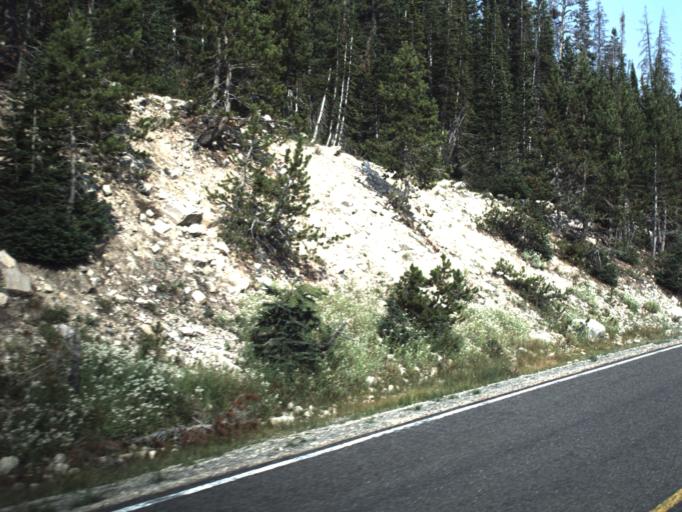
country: US
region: Utah
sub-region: Summit County
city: Kamas
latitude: 40.7132
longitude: -110.8891
